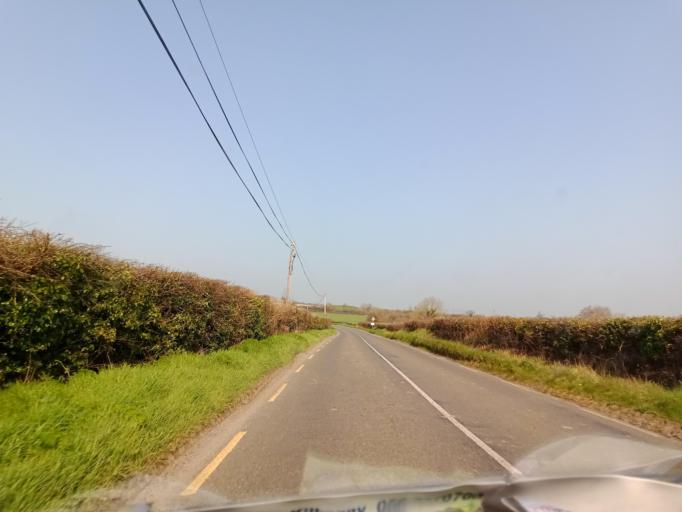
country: IE
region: Leinster
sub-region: Kilkenny
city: Callan
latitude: 52.5322
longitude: -7.3851
